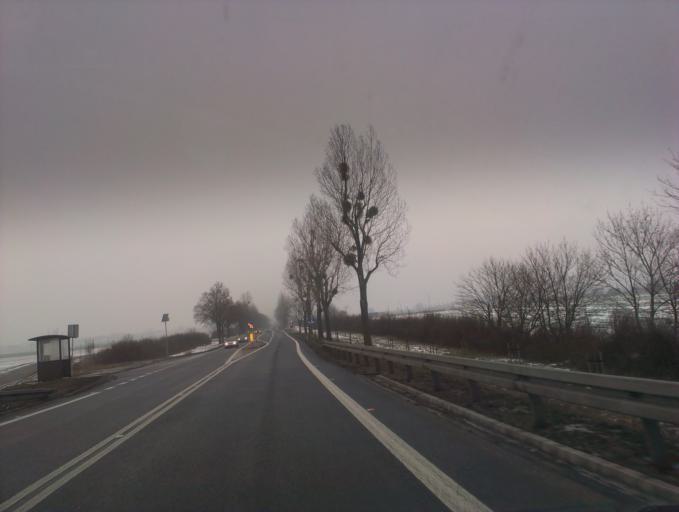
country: PL
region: Greater Poland Voivodeship
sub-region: Powiat obornicki
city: Oborniki
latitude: 52.6052
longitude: 16.8184
